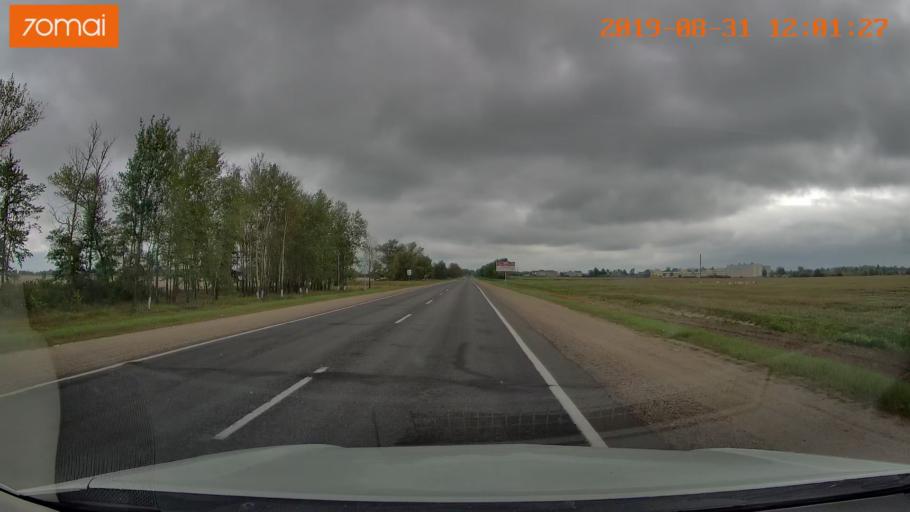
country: BY
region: Mogilev
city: Horad Krychaw
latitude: 53.6877
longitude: 31.6895
